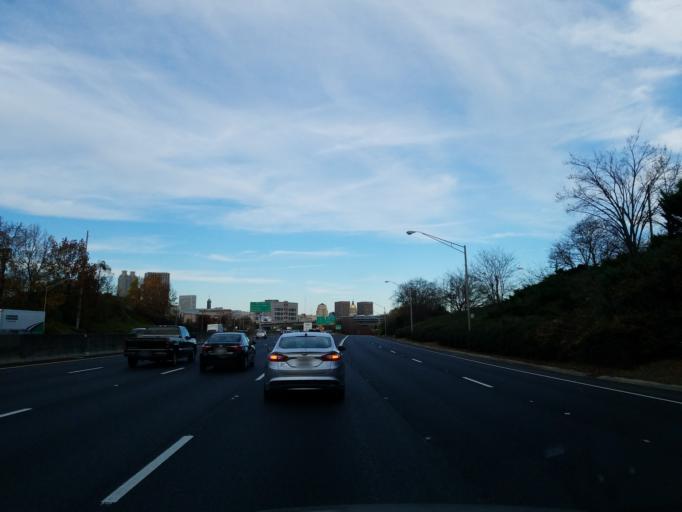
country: US
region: Georgia
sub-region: Fulton County
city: Atlanta
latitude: 33.7426
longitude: -84.4034
